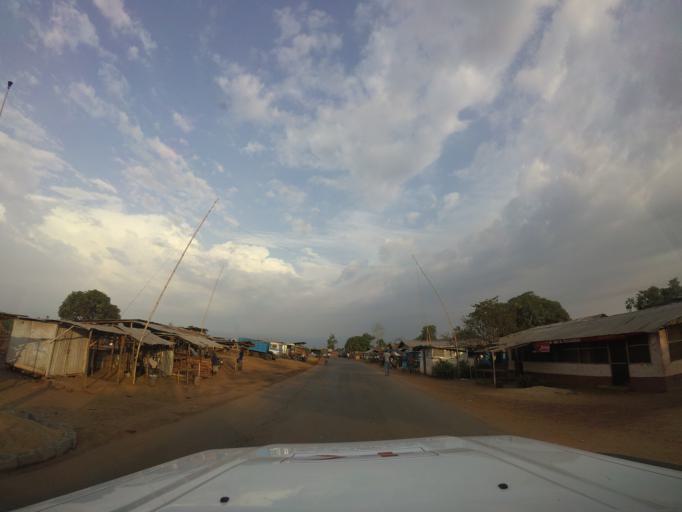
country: LR
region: Bomi
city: Tubmanburg
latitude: 6.7136
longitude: -10.9705
